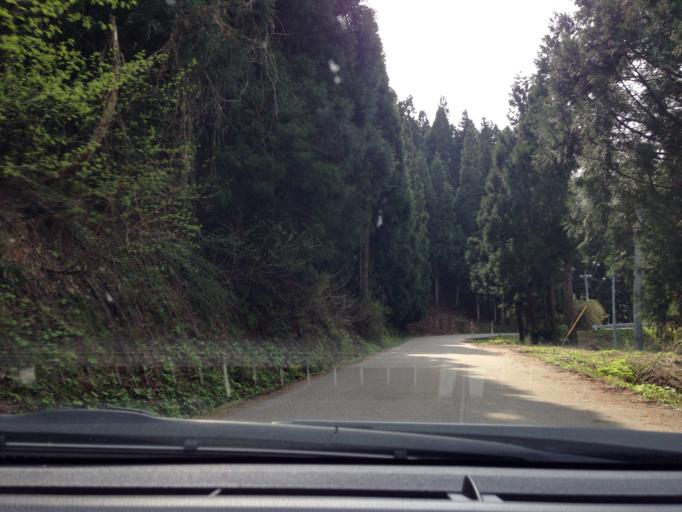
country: JP
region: Toyama
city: Fukumitsu
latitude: 36.4802
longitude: 136.8144
